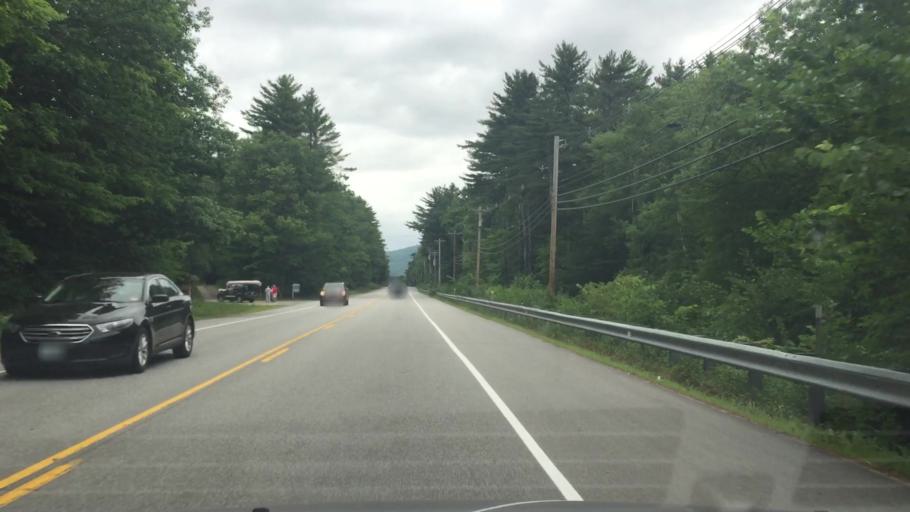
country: US
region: New Hampshire
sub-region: Carroll County
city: Center Harbor
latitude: 43.6903
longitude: -71.4585
